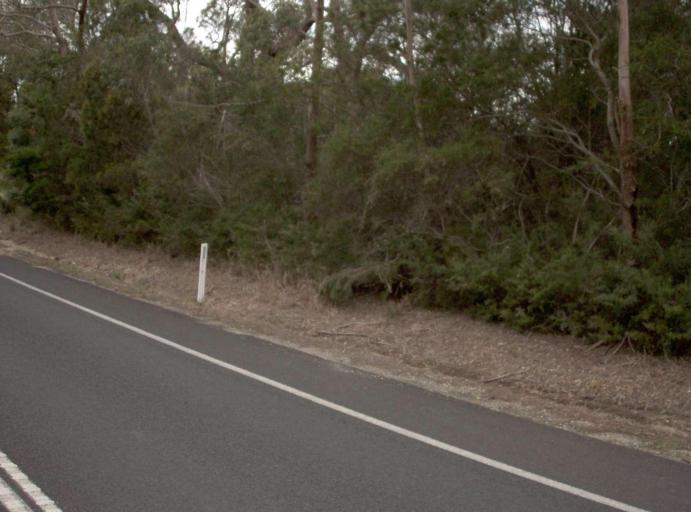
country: AU
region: Victoria
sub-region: Wellington
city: Sale
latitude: -38.1765
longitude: 147.0866
